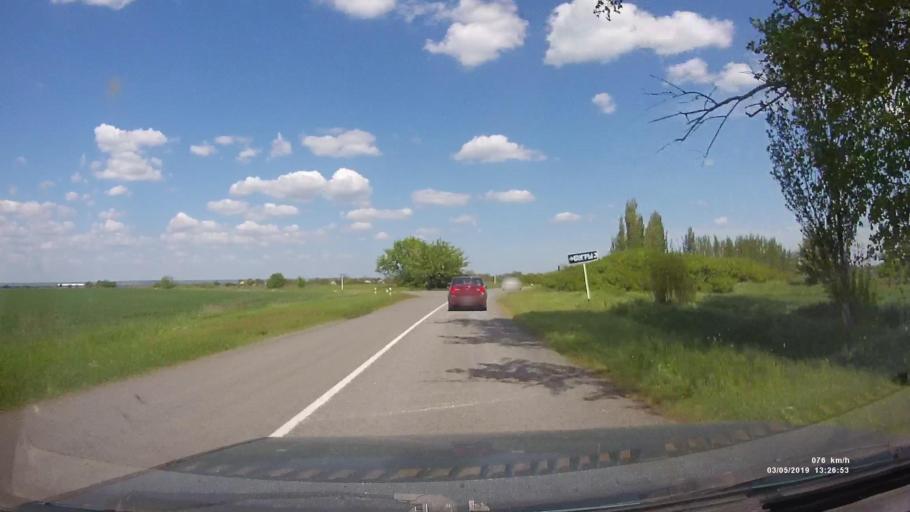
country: RU
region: Rostov
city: Semikarakorsk
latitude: 47.5744
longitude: 40.8264
